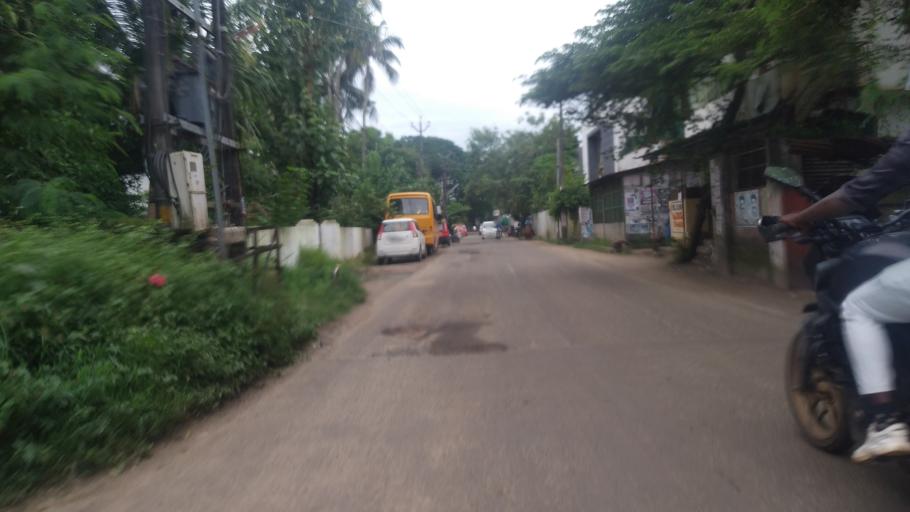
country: IN
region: Kerala
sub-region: Alappuzha
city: Arukutti
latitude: 9.8705
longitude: 76.2906
